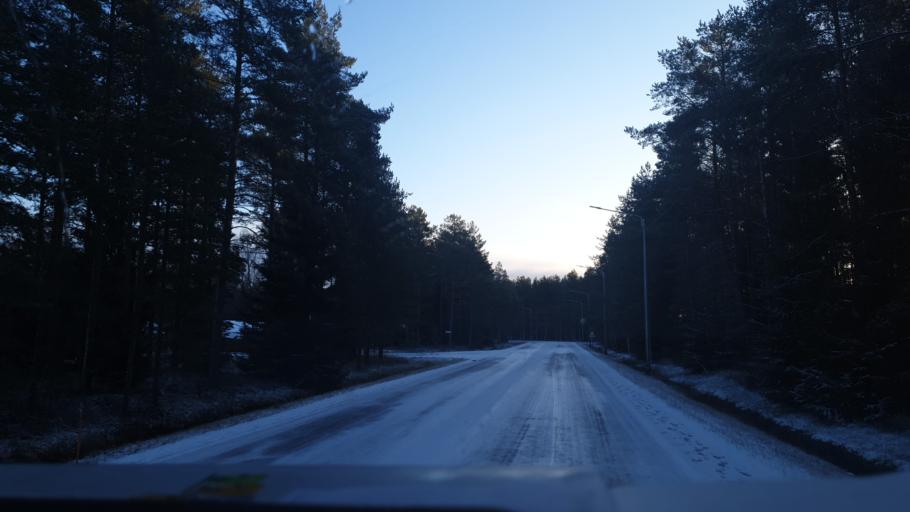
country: FI
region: Central Ostrobothnia
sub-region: Kokkola
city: Kokkola
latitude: 63.8211
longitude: 23.0693
